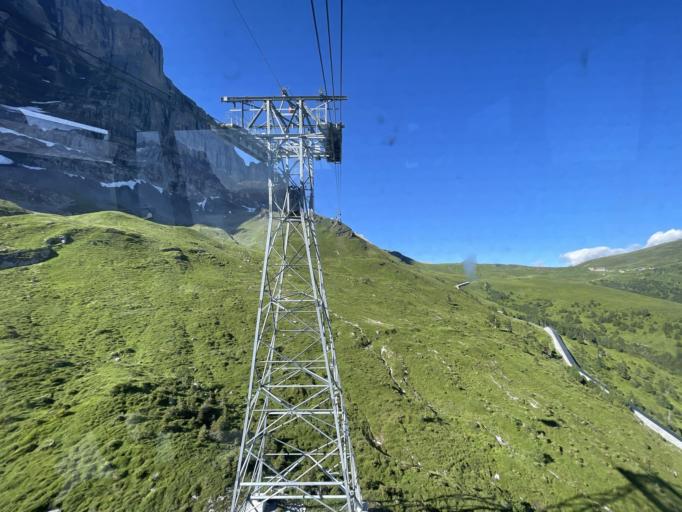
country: CH
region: Bern
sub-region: Interlaken-Oberhasli District
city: Grindelwald
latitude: 46.5902
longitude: 7.9888
